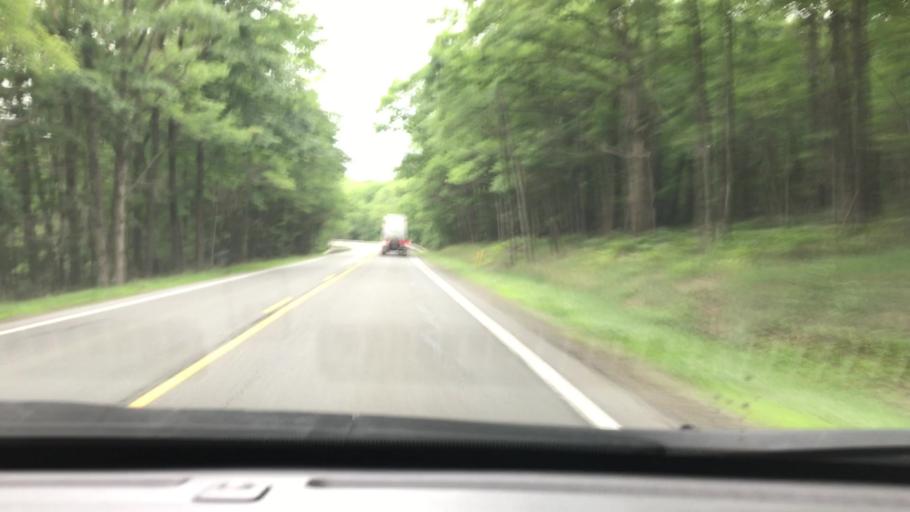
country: US
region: Pennsylvania
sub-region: Clearfield County
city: Treasure Lake
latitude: 41.2566
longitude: -78.6476
